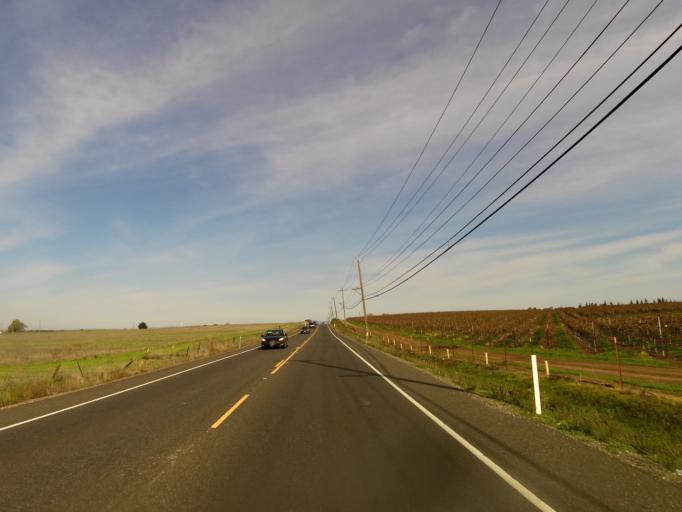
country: US
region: California
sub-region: Sacramento County
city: Wilton
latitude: 38.4777
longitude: -121.2506
